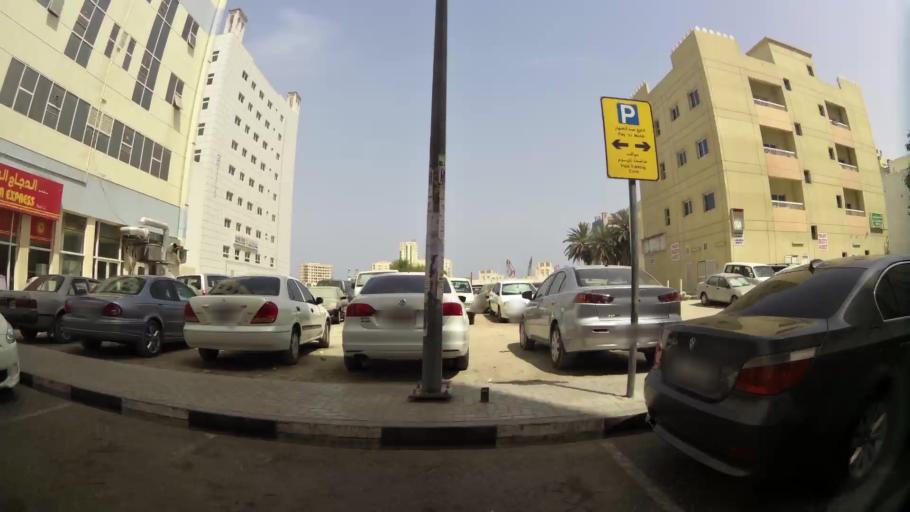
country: AE
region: Ash Shariqah
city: Sharjah
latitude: 25.3562
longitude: 55.3866
